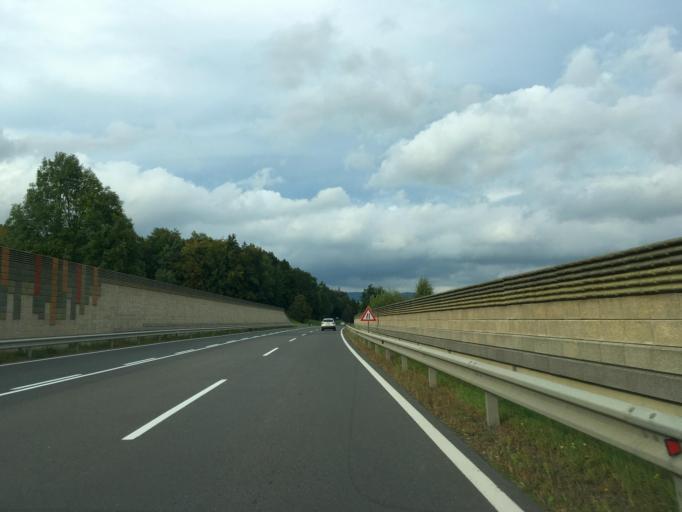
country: AT
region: Styria
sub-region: Politischer Bezirk Hartberg-Fuerstenfeld
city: Rohrbach an der Lafnitz
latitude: 47.4006
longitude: 16.0023
